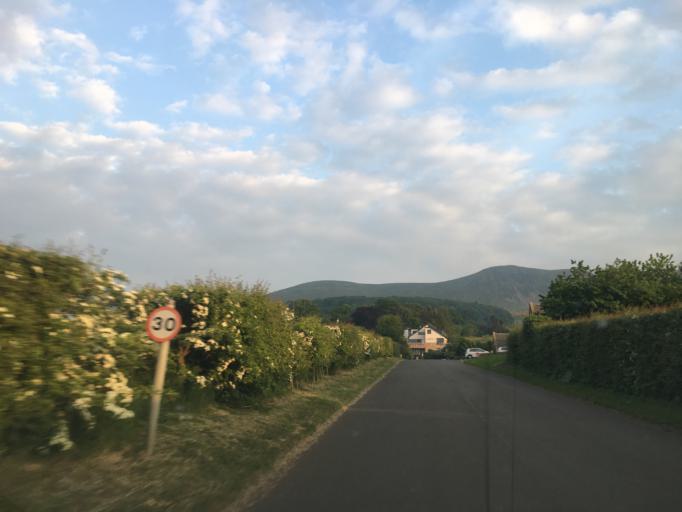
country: GB
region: Scotland
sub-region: Edinburgh
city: Colinton
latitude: 55.8958
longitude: -3.2170
